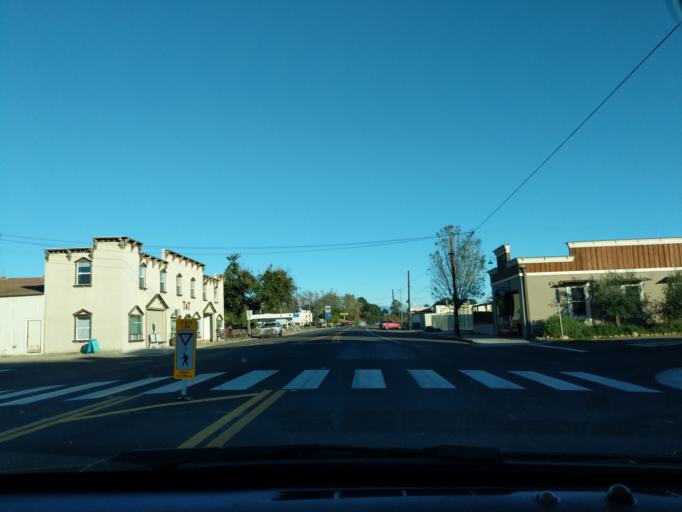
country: US
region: California
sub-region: Santa Barbara County
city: Los Alamos
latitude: 34.7440
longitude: -120.2780
